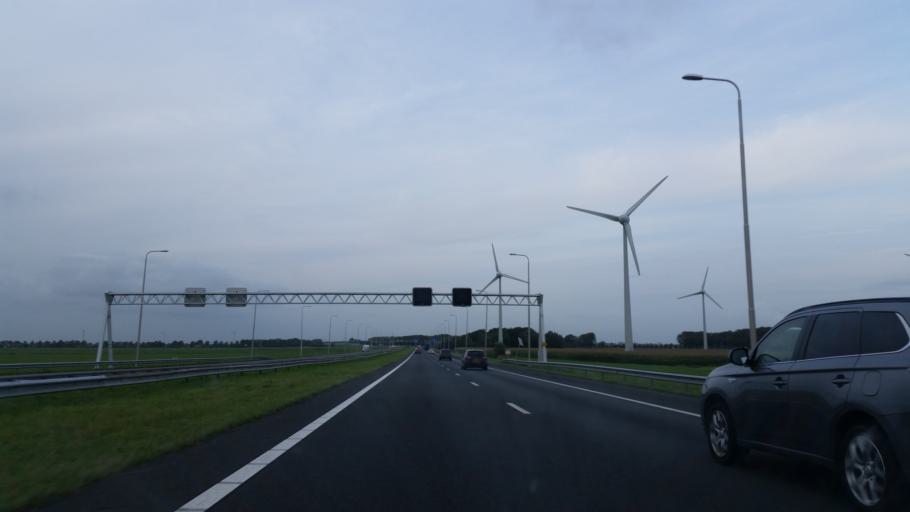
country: NL
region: North Holland
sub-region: Gemeente Hoorn
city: Hoorn
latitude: 52.6051
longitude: 4.9962
